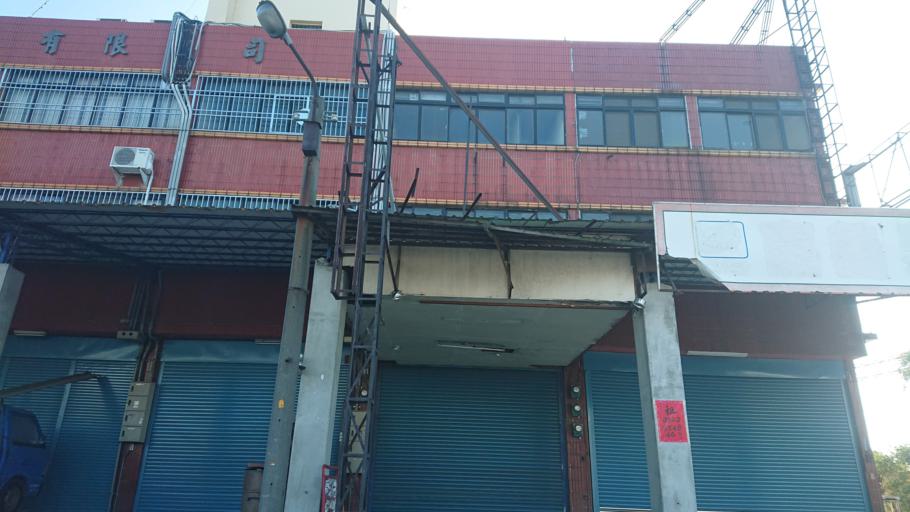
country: TW
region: Taiwan
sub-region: Changhua
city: Chang-hua
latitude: 24.1191
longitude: 120.5755
